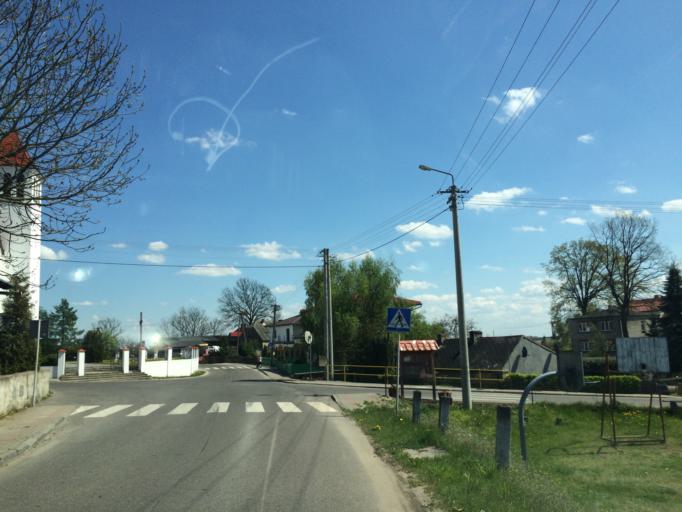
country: PL
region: Warmian-Masurian Voivodeship
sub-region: Powiat nowomiejski
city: Kurzetnik
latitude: 53.3849
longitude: 19.4668
